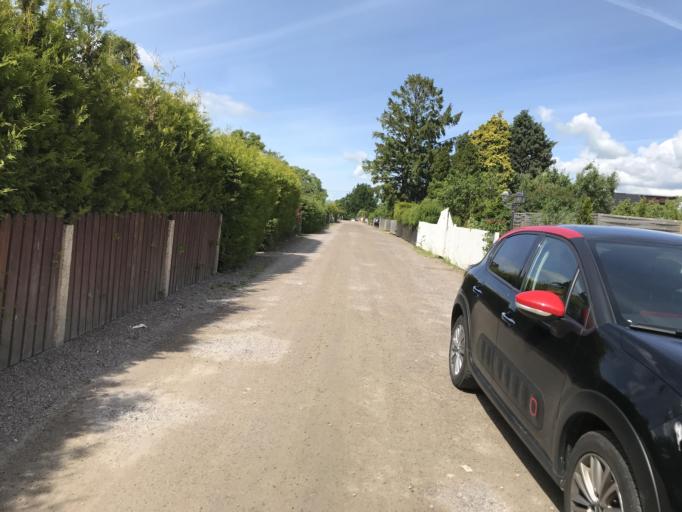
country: SE
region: Skane
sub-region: Landskrona
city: Landskrona
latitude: 55.8963
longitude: 12.8372
